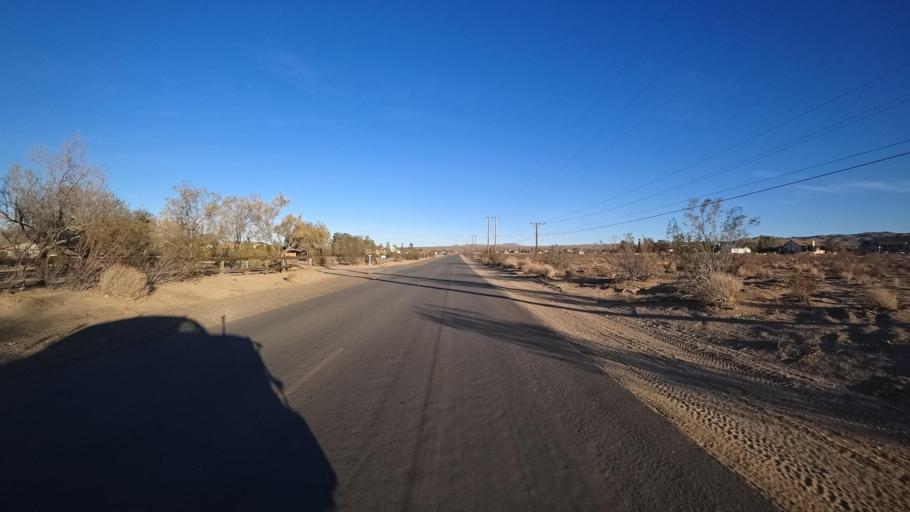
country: US
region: California
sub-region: Kern County
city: Ridgecrest
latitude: 35.5935
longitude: -117.6654
